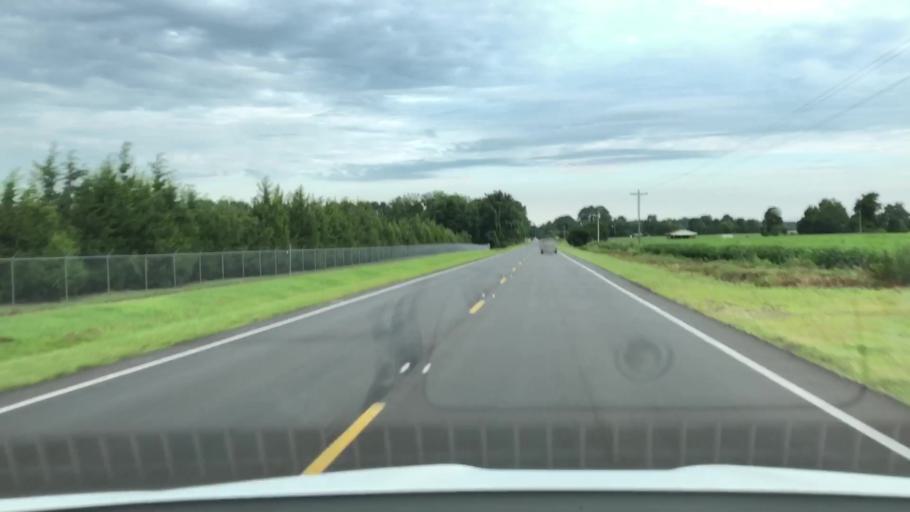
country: US
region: North Carolina
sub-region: Jones County
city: Maysville
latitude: 34.8936
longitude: -77.2171
